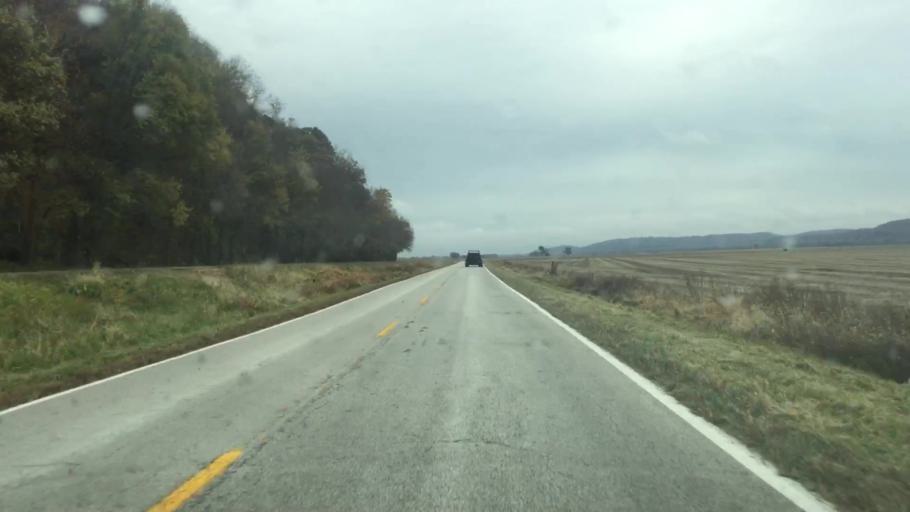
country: US
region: Missouri
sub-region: Gasconade County
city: Hermann
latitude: 38.7034
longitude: -91.5664
